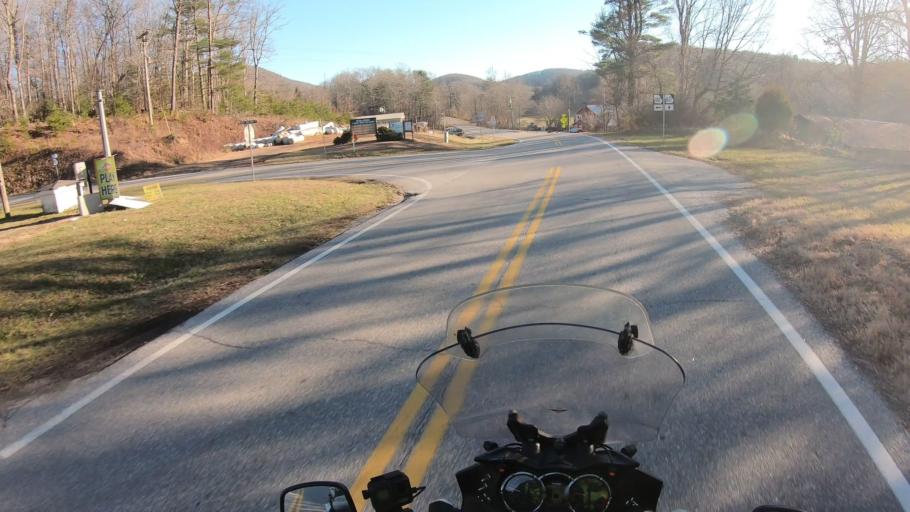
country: US
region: Georgia
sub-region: Lumpkin County
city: Dahlonega
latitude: 34.6976
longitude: -84.0294
